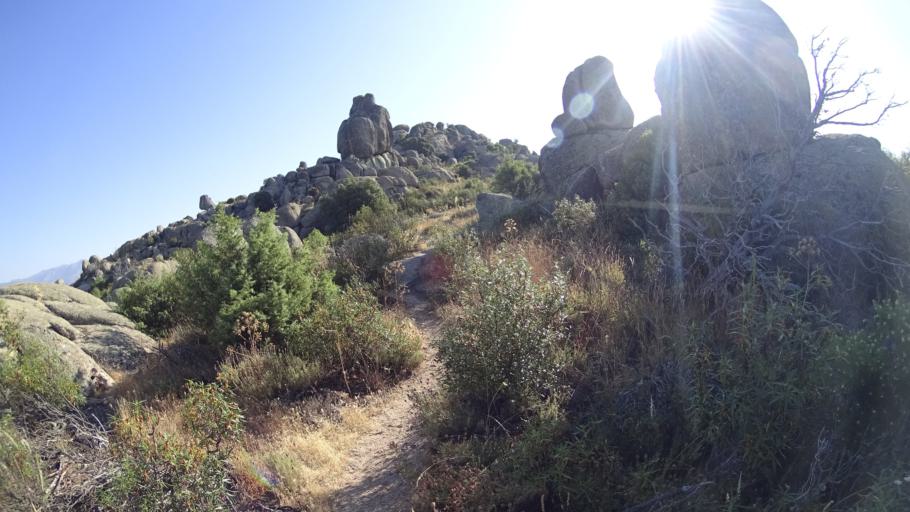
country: ES
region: Madrid
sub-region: Provincia de Madrid
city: Moralzarzal
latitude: 40.6498
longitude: -3.9506
